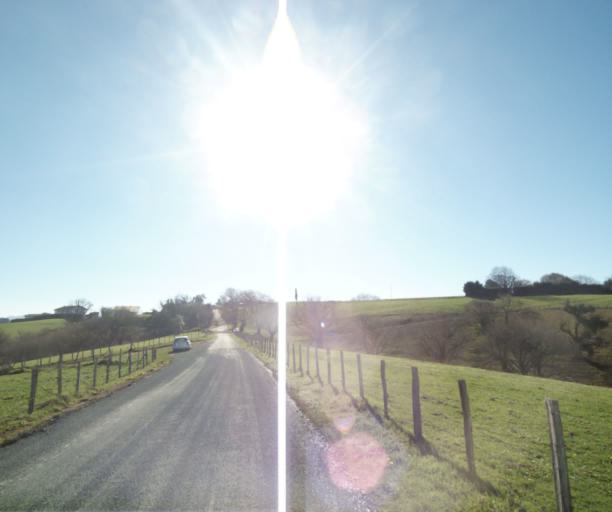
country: FR
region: Aquitaine
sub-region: Departement des Pyrenees-Atlantiques
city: Urrugne
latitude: 43.3717
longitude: -1.7243
